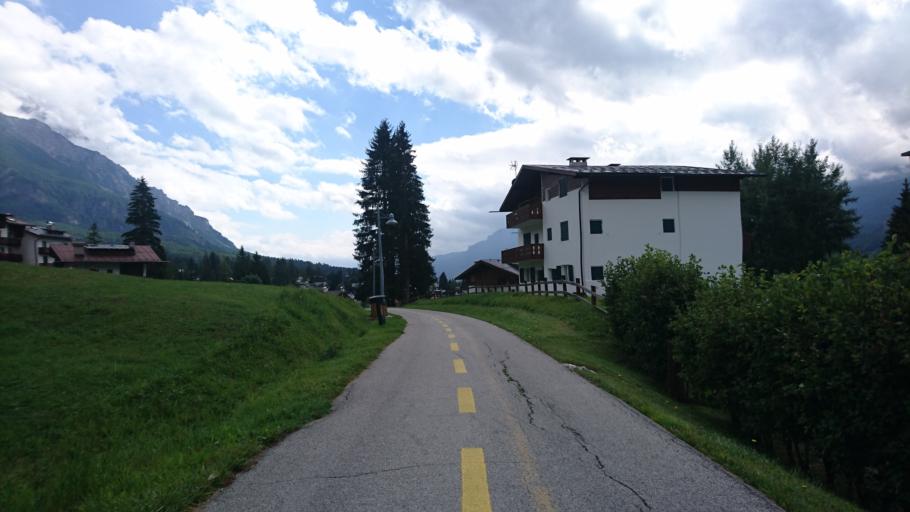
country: IT
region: Veneto
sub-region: Provincia di Belluno
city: Cortina d'Ampezzo
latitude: 46.5472
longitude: 12.1345
